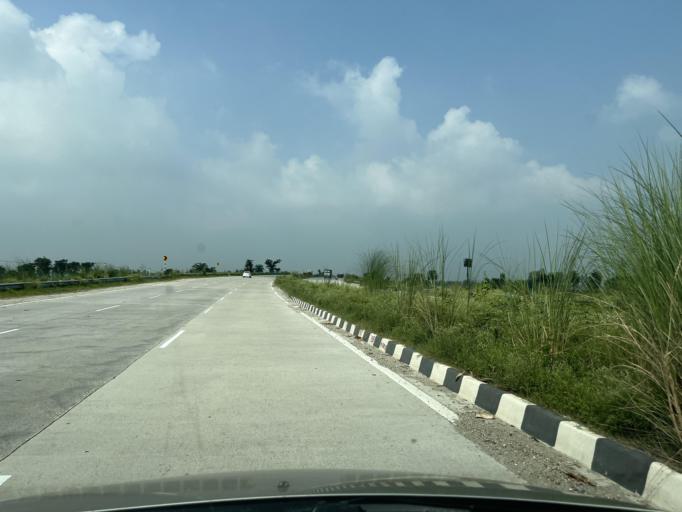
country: IN
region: Uttarakhand
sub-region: Udham Singh Nagar
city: Kashipur
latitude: 29.1636
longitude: 78.9676
